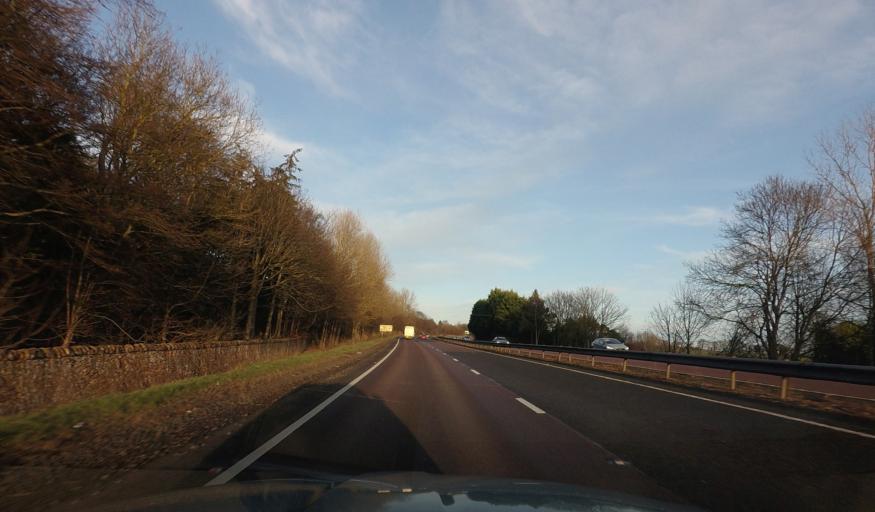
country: GB
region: Scotland
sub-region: Perth and Kinross
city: Errol
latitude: 56.4542
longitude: -3.1494
